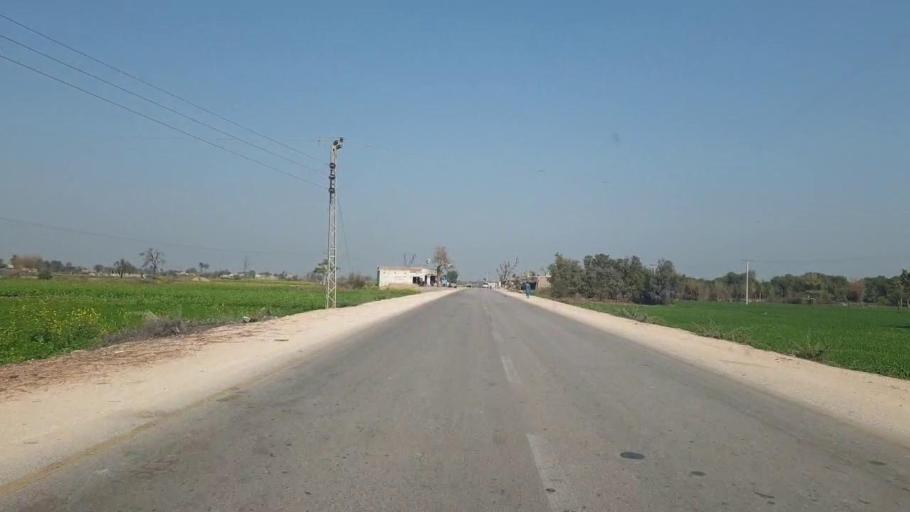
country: PK
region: Sindh
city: Sakrand
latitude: 26.0264
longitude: 68.3989
